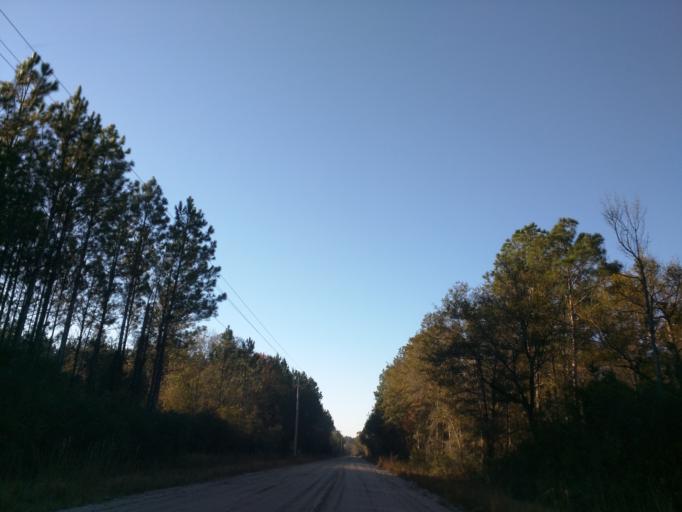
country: US
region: Florida
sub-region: Leon County
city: Woodville
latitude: 30.2522
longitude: -84.1675
